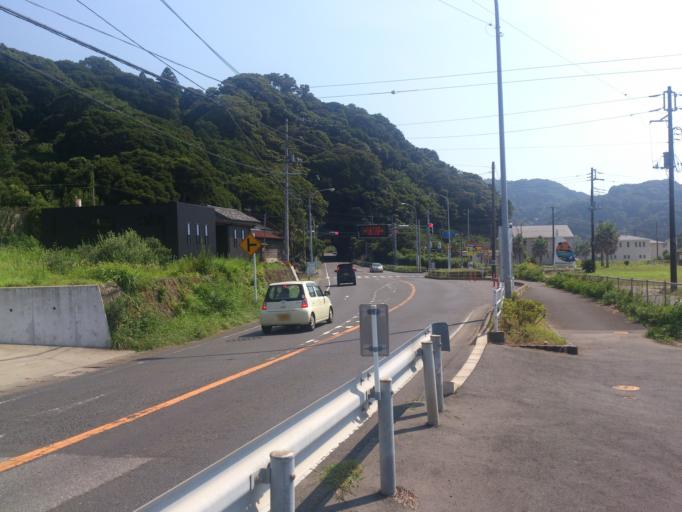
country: JP
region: Chiba
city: Tateyama
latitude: 35.0814
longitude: 139.8408
